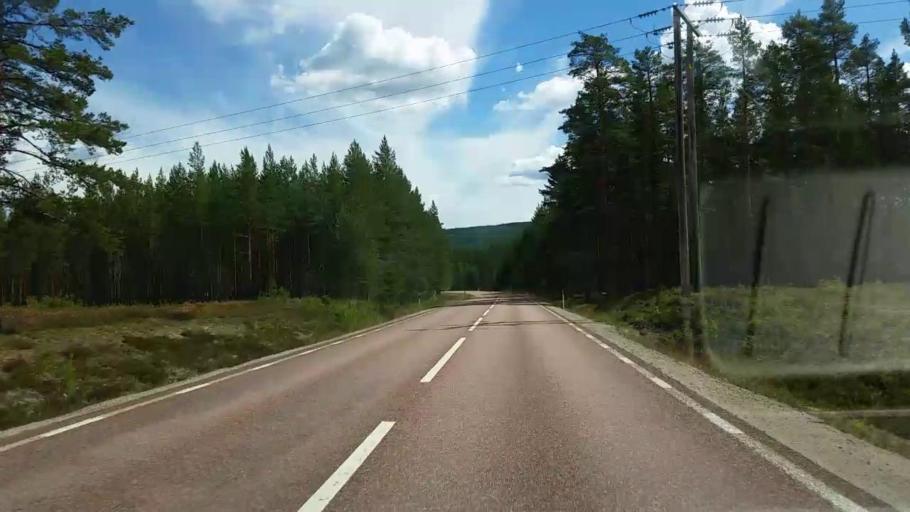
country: SE
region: Gaevleborg
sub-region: Ovanakers Kommun
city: Edsbyn
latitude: 61.3491
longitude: 15.5912
